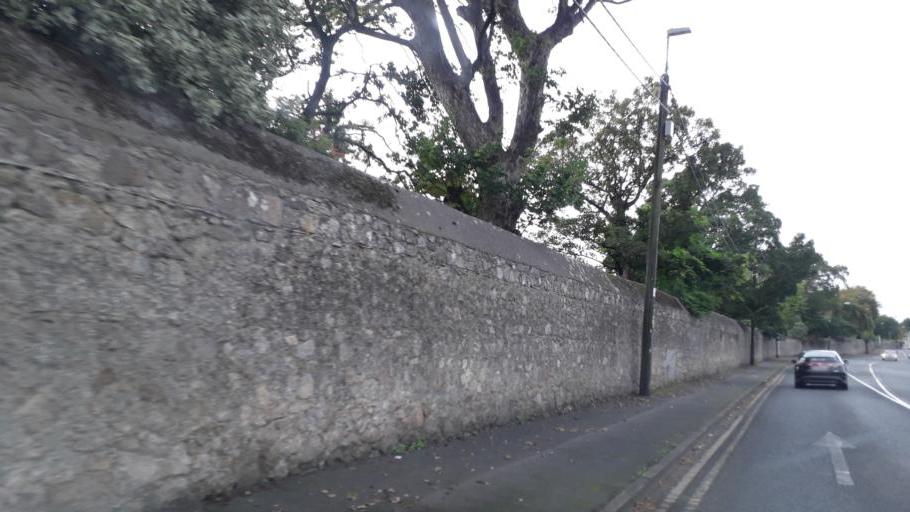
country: IE
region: Leinster
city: Cabinteely
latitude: 53.2652
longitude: -6.1604
